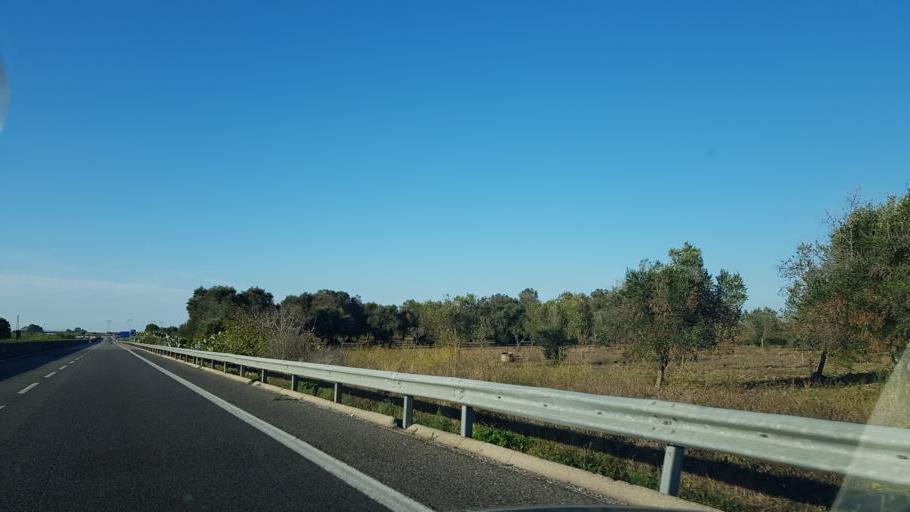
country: IT
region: Apulia
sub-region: Provincia di Brindisi
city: Tuturano
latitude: 40.5437
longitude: 18.0009
